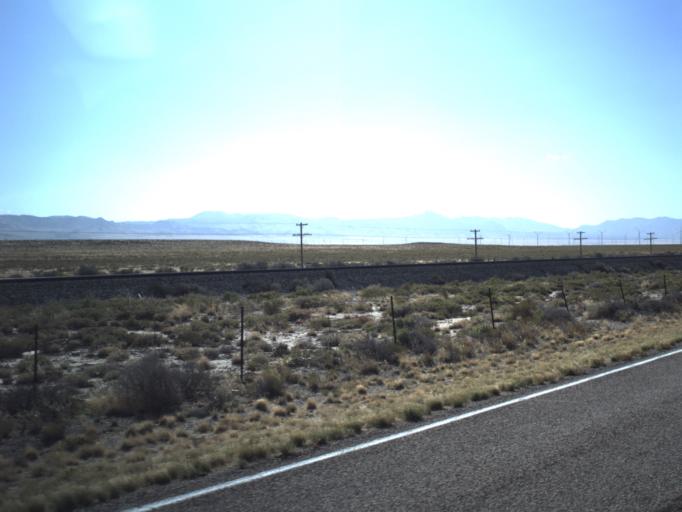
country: US
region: Utah
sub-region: Beaver County
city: Milford
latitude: 38.6365
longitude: -112.9837
